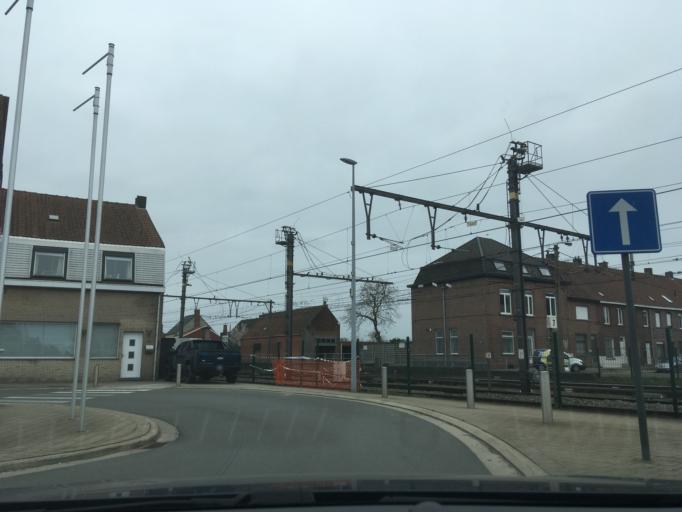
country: BE
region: Flanders
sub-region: Provincie West-Vlaanderen
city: Lichtervelde
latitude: 51.0245
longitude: 3.1285
